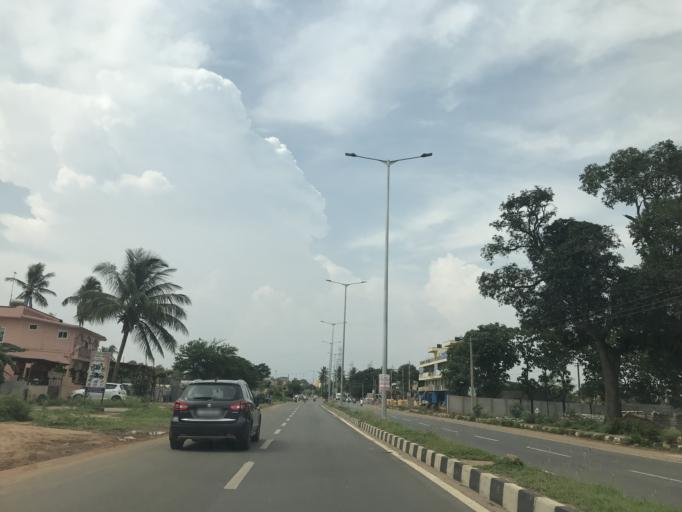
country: IN
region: Karnataka
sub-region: Bangalore Urban
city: Yelahanka
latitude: 13.1375
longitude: 77.6695
